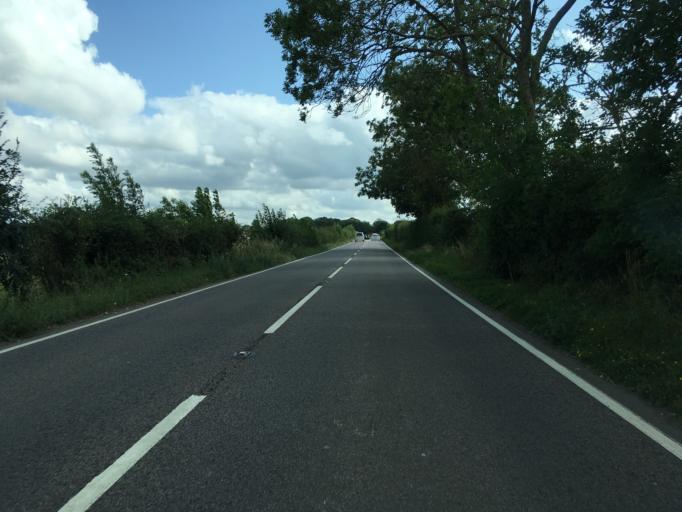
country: GB
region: England
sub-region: Kent
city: Headcorn
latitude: 51.1597
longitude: 0.6332
